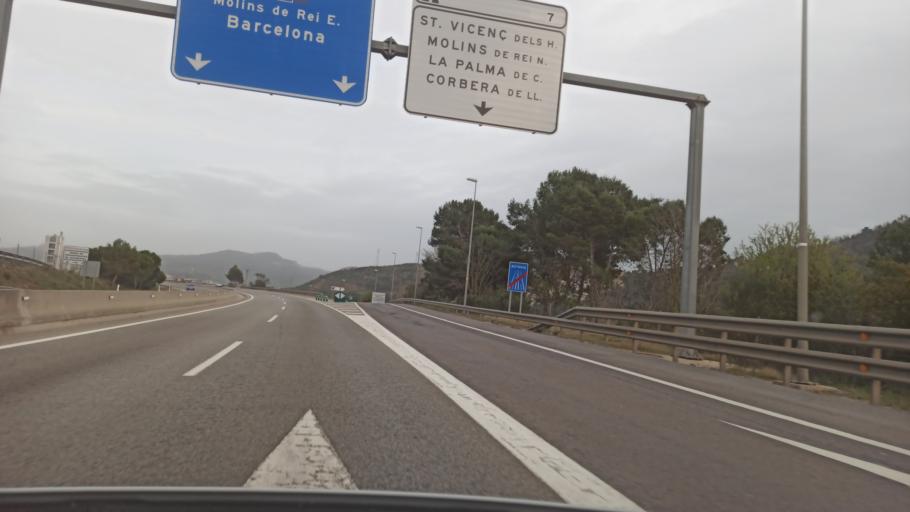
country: ES
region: Catalonia
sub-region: Provincia de Barcelona
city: Cervello
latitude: 41.3991
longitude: 1.9805
